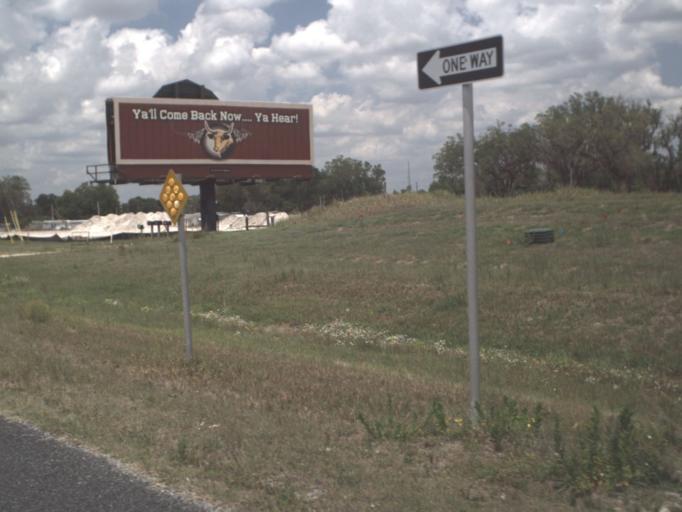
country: US
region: Florida
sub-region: Sumter County
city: Wildwood
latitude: 28.8456
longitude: -82.0349
